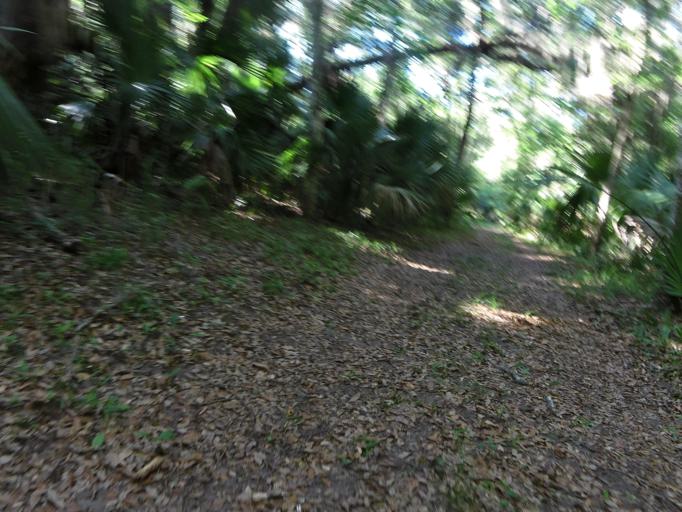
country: US
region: Florida
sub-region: Duval County
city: Atlantic Beach
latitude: 30.4420
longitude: -81.4694
